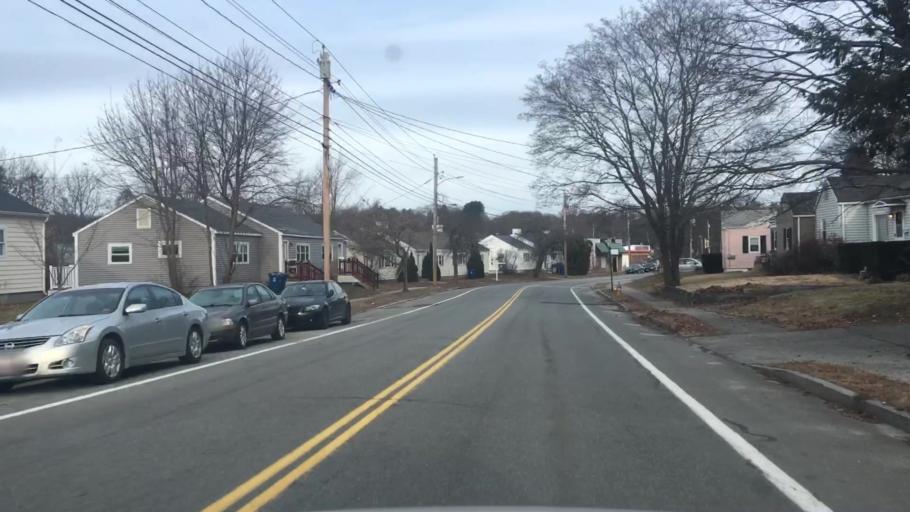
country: US
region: Maine
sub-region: Cumberland County
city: Portland
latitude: 43.6614
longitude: -70.2841
